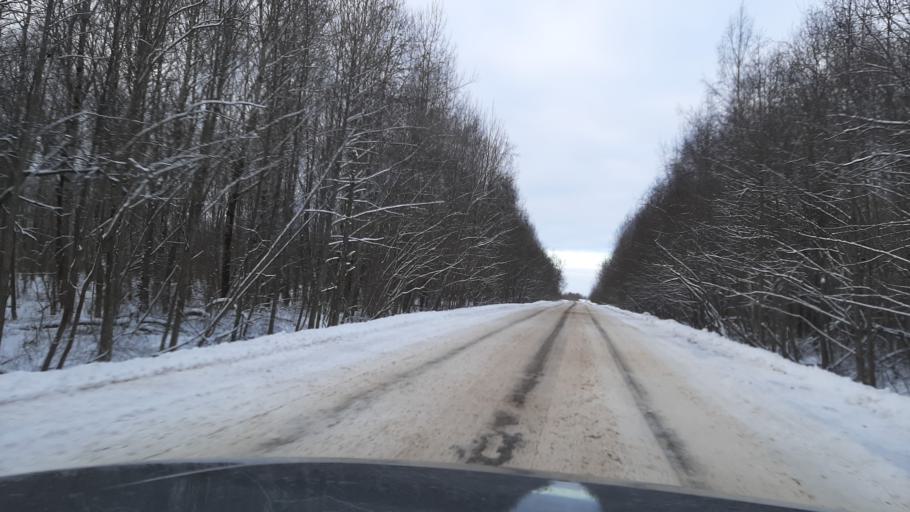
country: RU
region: Kostroma
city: Kosmynino
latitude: 57.4809
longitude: 40.7552
